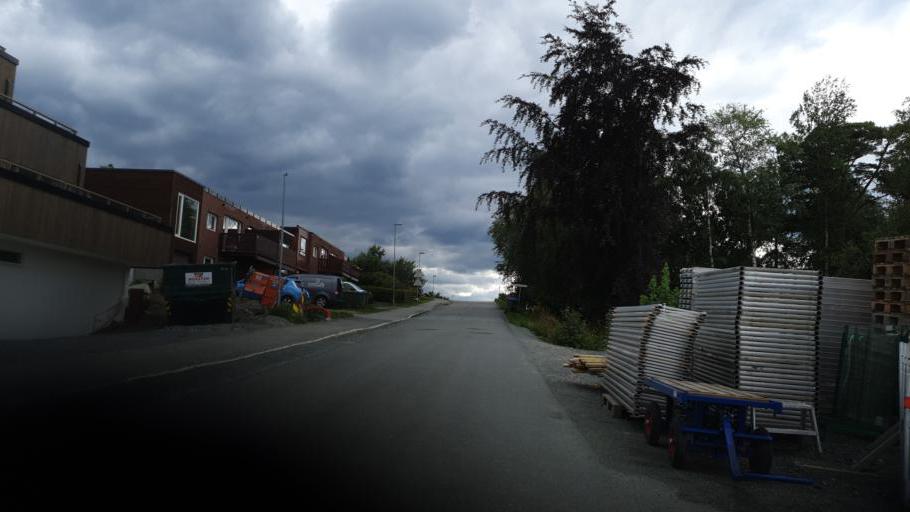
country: NO
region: Sor-Trondelag
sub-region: Malvik
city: Malvik
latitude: 63.4391
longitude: 10.5957
